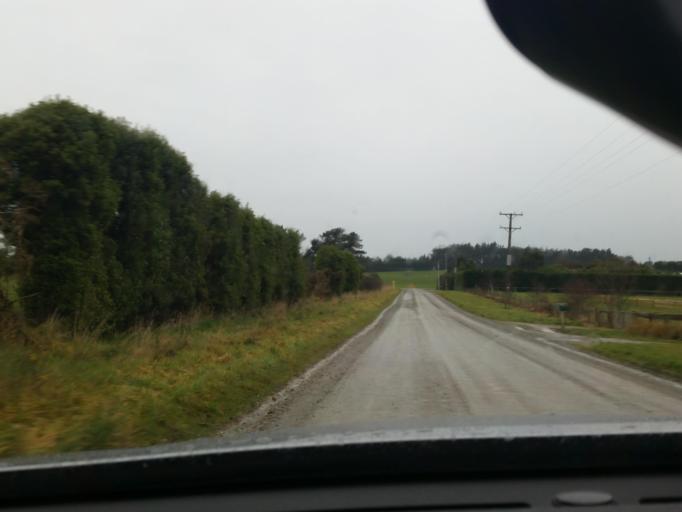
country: NZ
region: Southland
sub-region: Invercargill City
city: Invercargill
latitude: -46.3557
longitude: 168.4492
